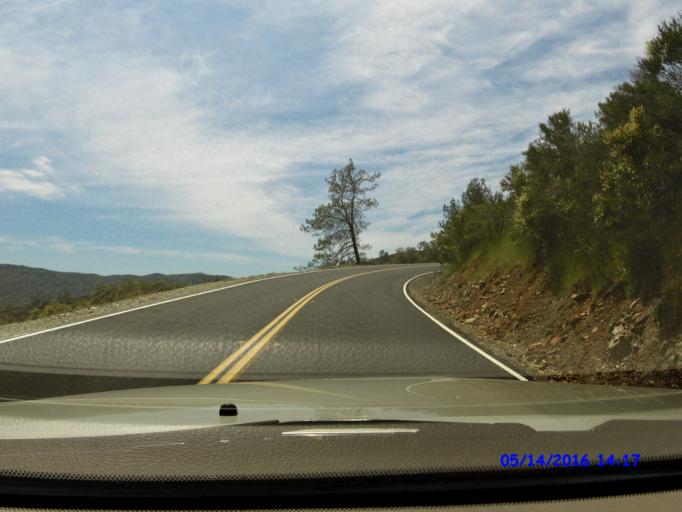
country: US
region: California
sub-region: Mariposa County
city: Mariposa
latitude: 37.6632
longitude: -120.1496
